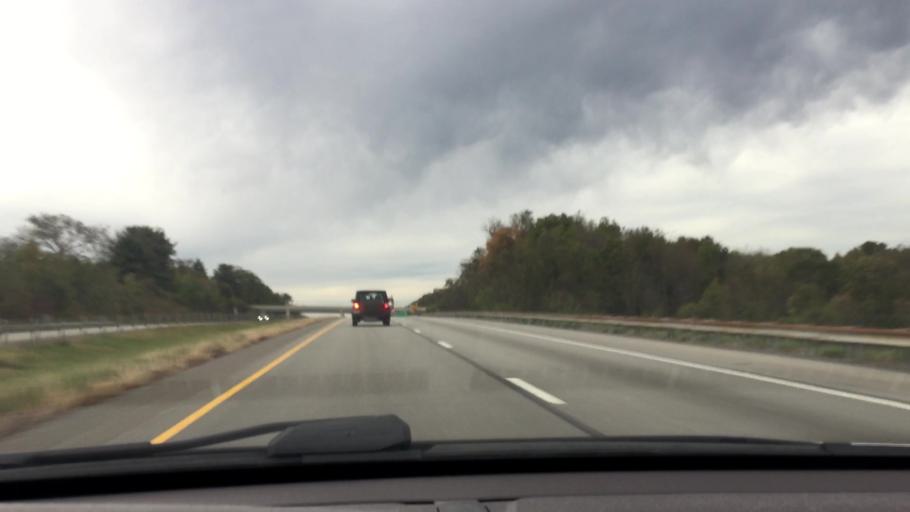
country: US
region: Pennsylvania
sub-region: Beaver County
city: Beaver
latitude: 40.6941
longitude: -80.3584
